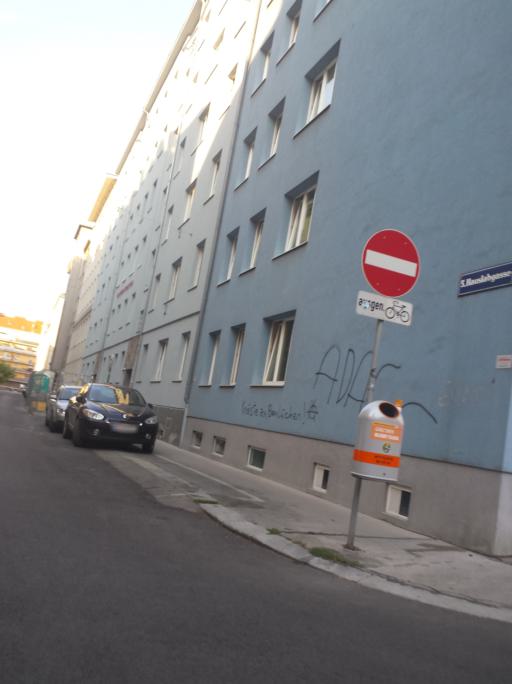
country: AT
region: Vienna
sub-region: Wien Stadt
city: Vienna
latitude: 48.1836
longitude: 16.3618
